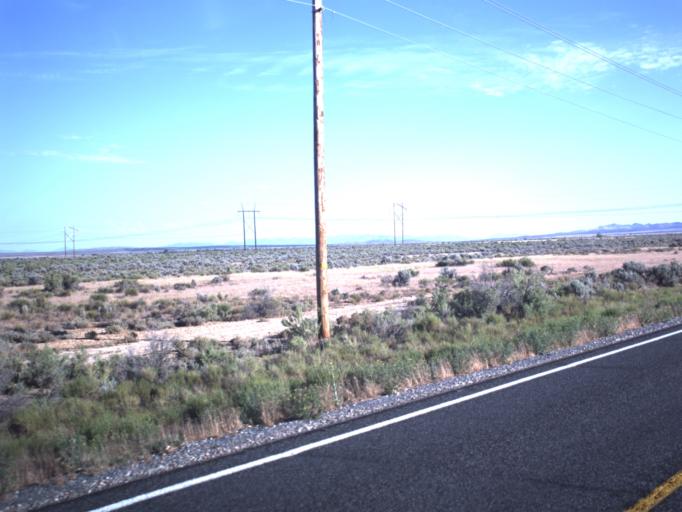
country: US
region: Utah
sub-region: Iron County
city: Enoch
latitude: 37.7991
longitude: -113.0506
